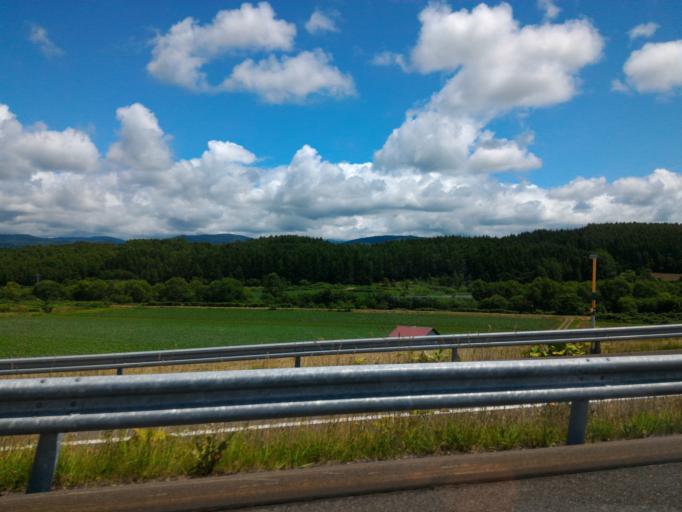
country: JP
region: Hokkaido
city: Nayoro
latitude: 44.4162
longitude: 142.4023
